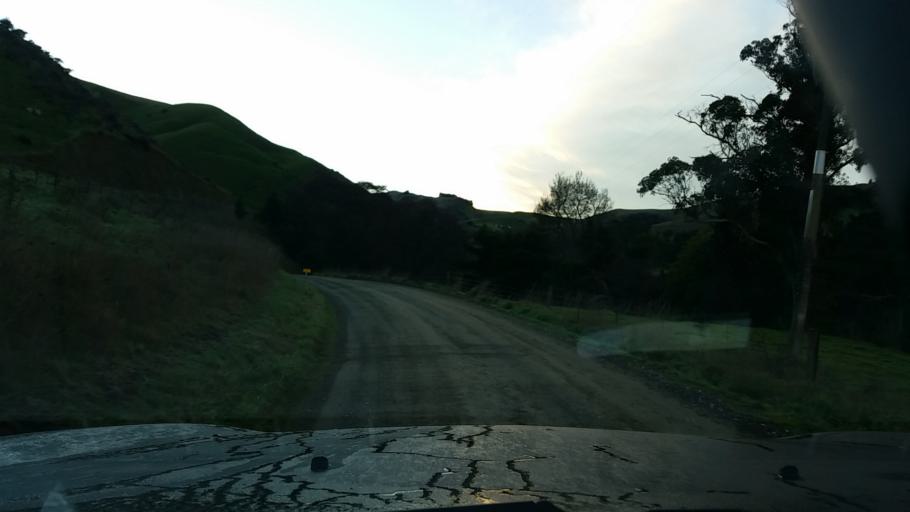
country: NZ
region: Marlborough
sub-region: Marlborough District
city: Blenheim
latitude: -41.5753
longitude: 173.9440
